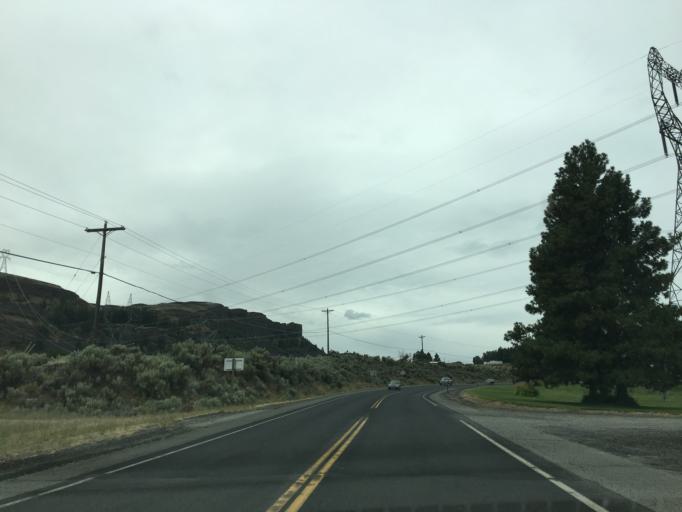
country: US
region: Washington
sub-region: Okanogan County
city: Coulee Dam
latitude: 47.9381
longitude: -119.0125
